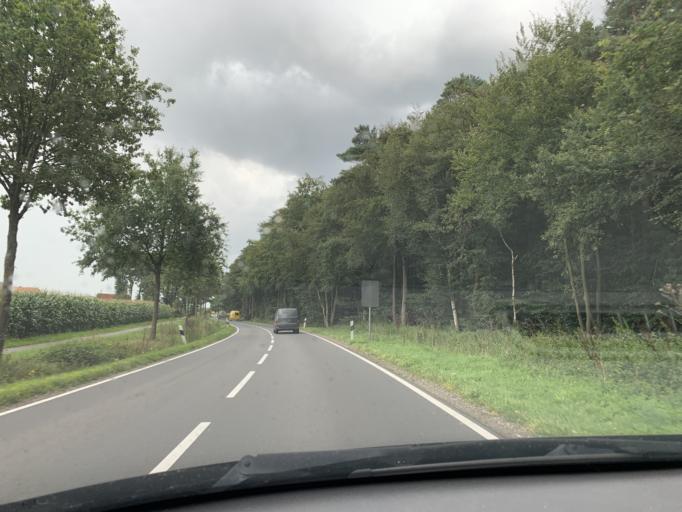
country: DE
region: Lower Saxony
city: Westerstede
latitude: 53.2860
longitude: 8.0015
